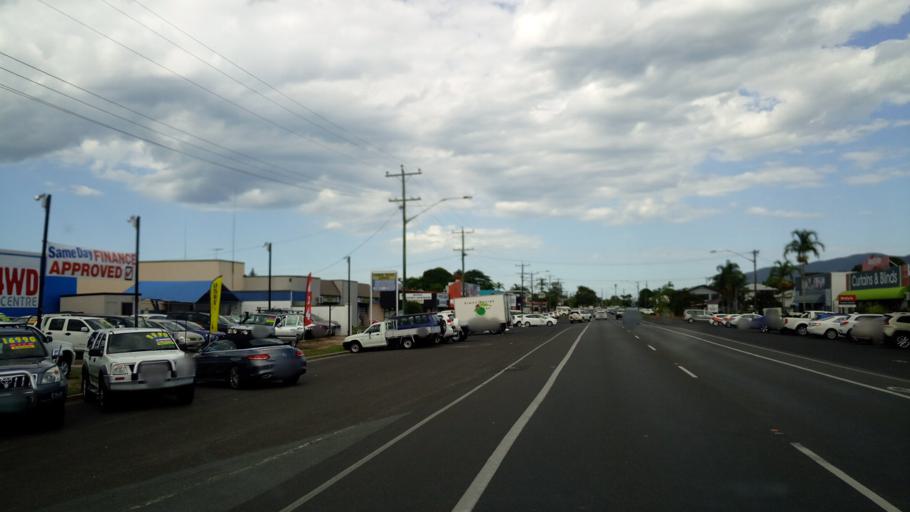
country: AU
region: Queensland
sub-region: Cairns
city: Cairns
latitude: -16.9360
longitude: 145.7576
